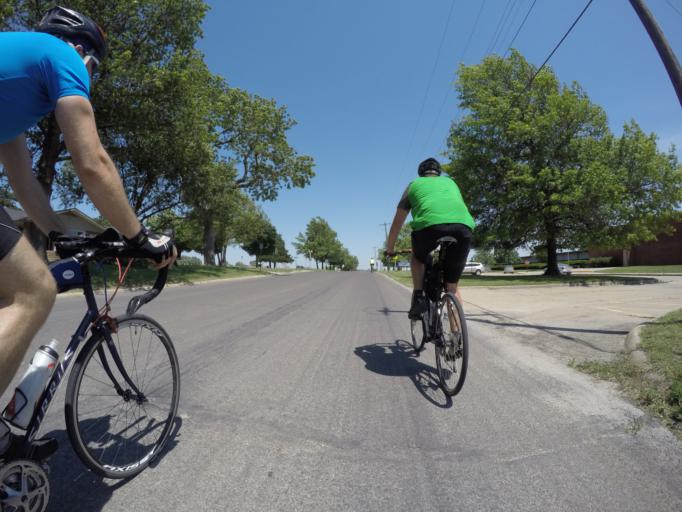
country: US
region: Kansas
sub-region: Nemaha County
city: Sabetha
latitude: 39.8997
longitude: -95.7920
